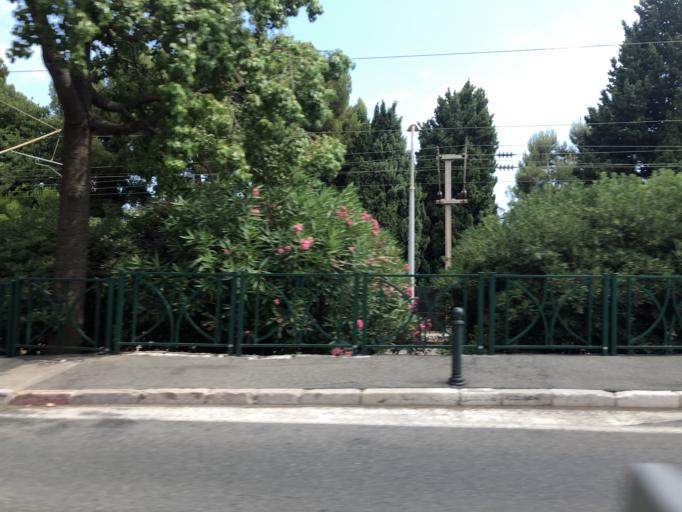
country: FR
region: Provence-Alpes-Cote d'Azur
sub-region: Departement des Alpes-Maritimes
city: Eze
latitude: 43.7218
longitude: 7.3556
